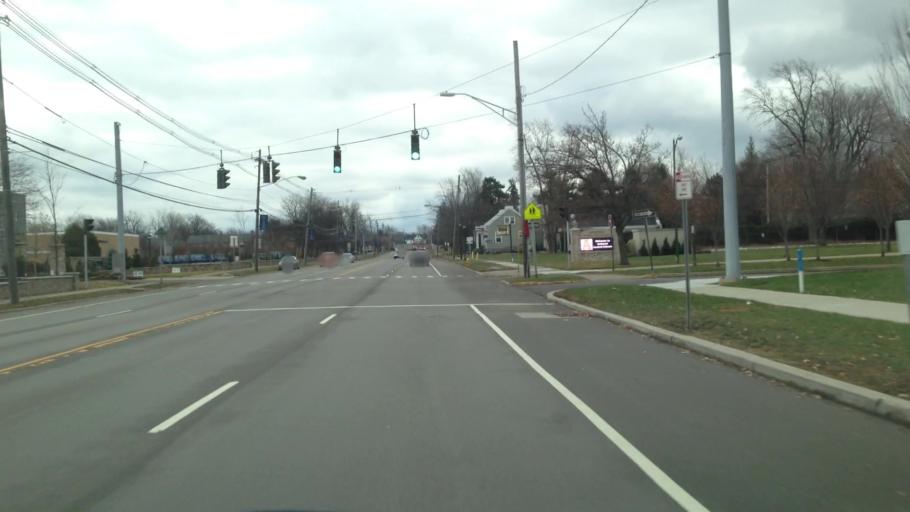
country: US
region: New York
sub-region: Erie County
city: Eggertsville
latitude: 42.9638
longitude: -78.7908
